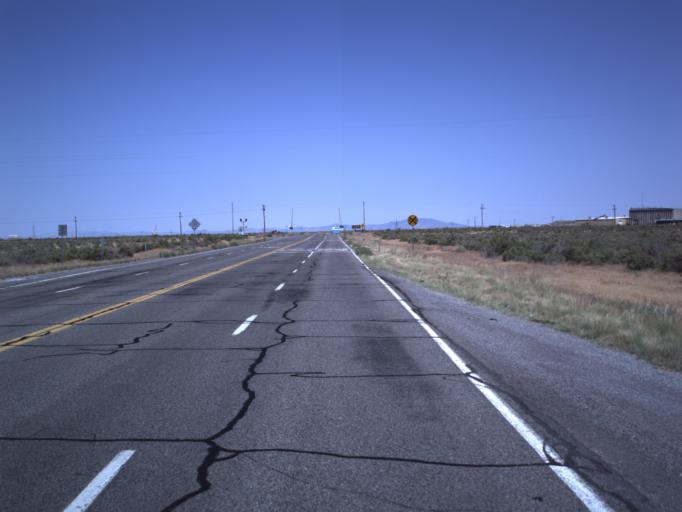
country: US
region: Utah
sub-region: Millard County
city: Delta
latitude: 39.4626
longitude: -112.4343
